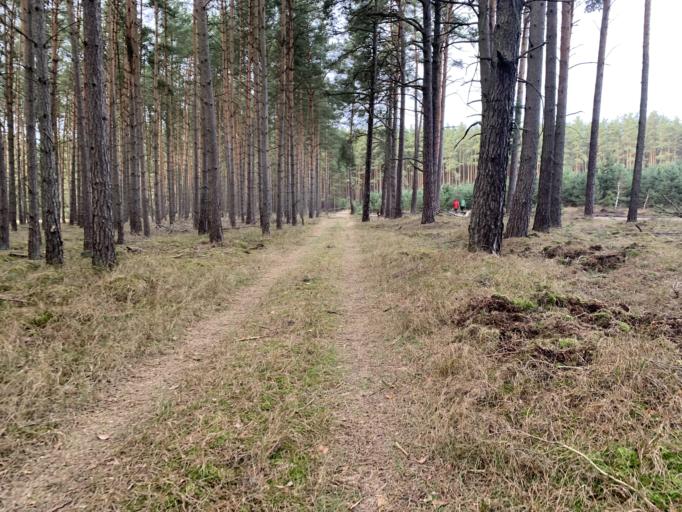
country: DE
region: Mecklenburg-Vorpommern
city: Wesenberg
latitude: 53.2888
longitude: 12.8769
